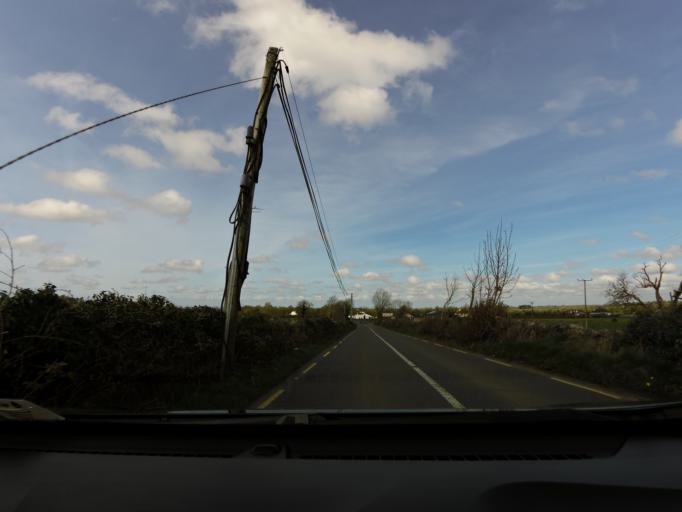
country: IE
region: Connaught
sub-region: County Galway
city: Athenry
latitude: 53.3129
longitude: -8.8026
